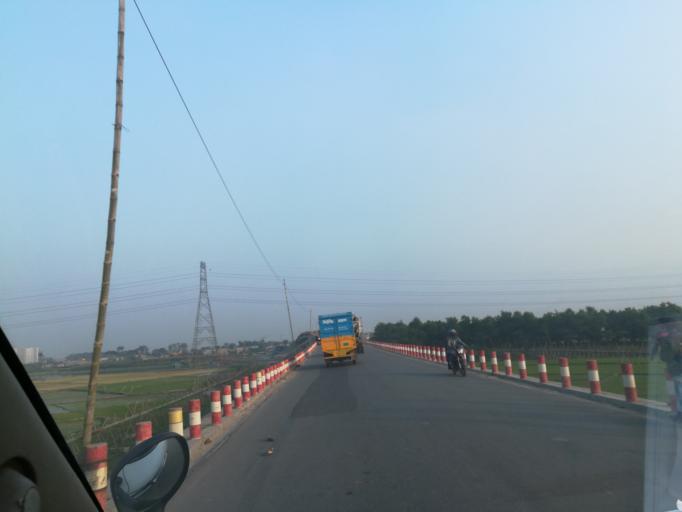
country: BD
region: Dhaka
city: Tungi
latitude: 23.8532
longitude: 90.3360
